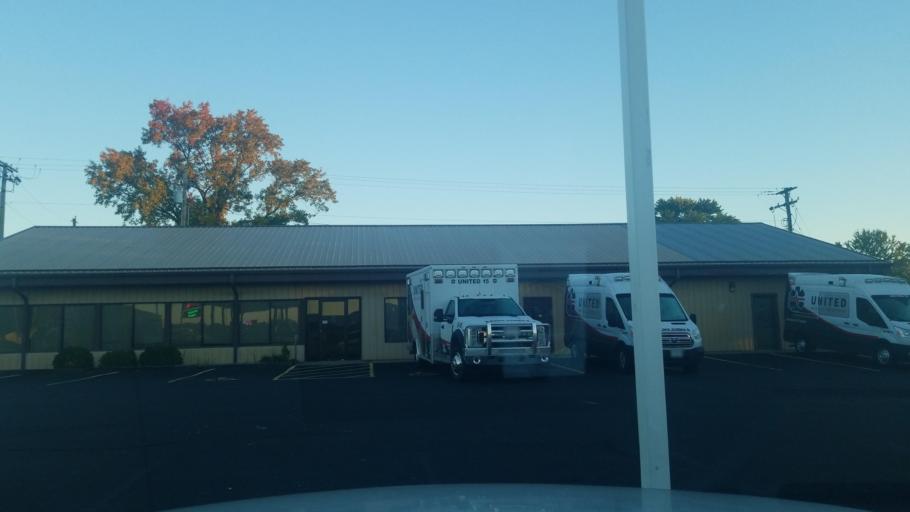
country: US
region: Illinois
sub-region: Williamson County
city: Energy
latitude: 37.7486
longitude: -89.0211
